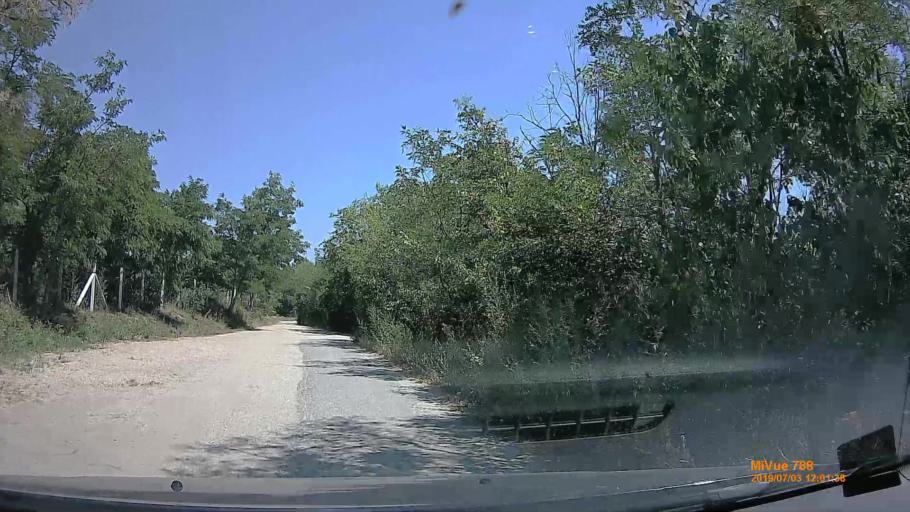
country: HU
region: Gyor-Moson-Sopron
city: Gyor
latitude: 47.7166
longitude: 17.6145
